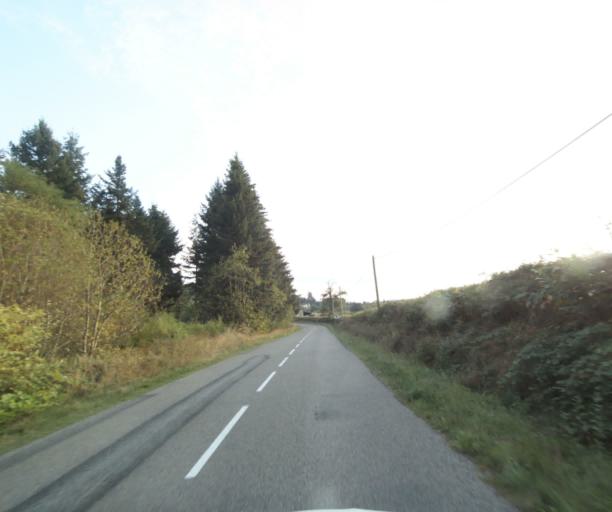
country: FR
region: Bourgogne
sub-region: Departement de Saone-et-Loire
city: Charolles
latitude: 46.4131
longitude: 4.4033
